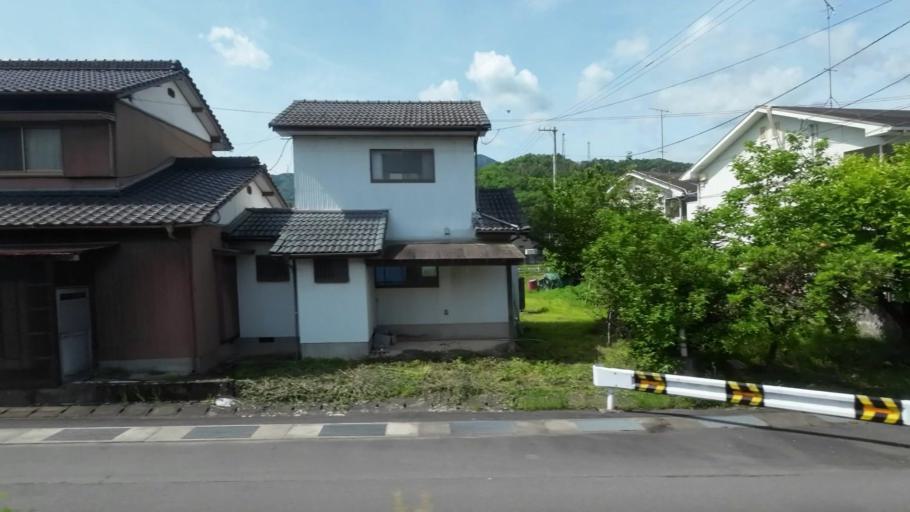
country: JP
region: Tokushima
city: Wakimachi
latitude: 34.0578
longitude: 134.2207
